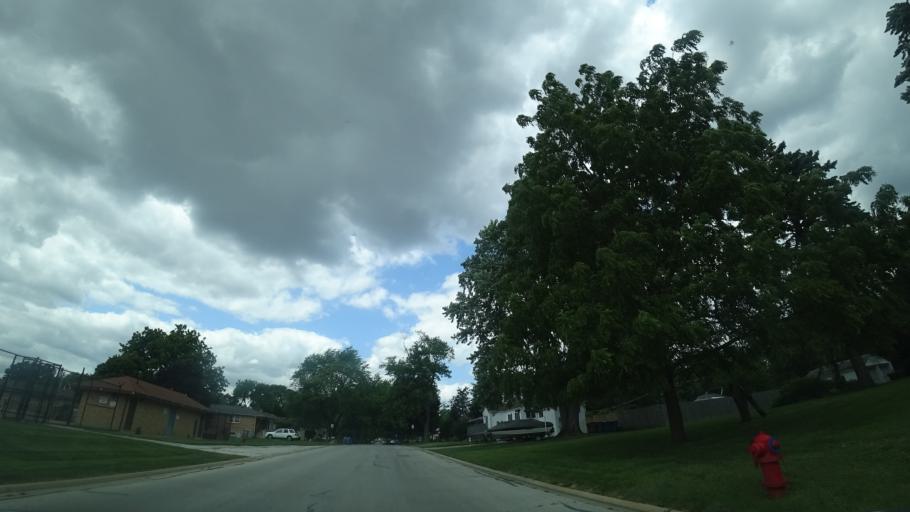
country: US
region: Illinois
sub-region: Cook County
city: Alsip
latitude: 41.6804
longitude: -87.7224
